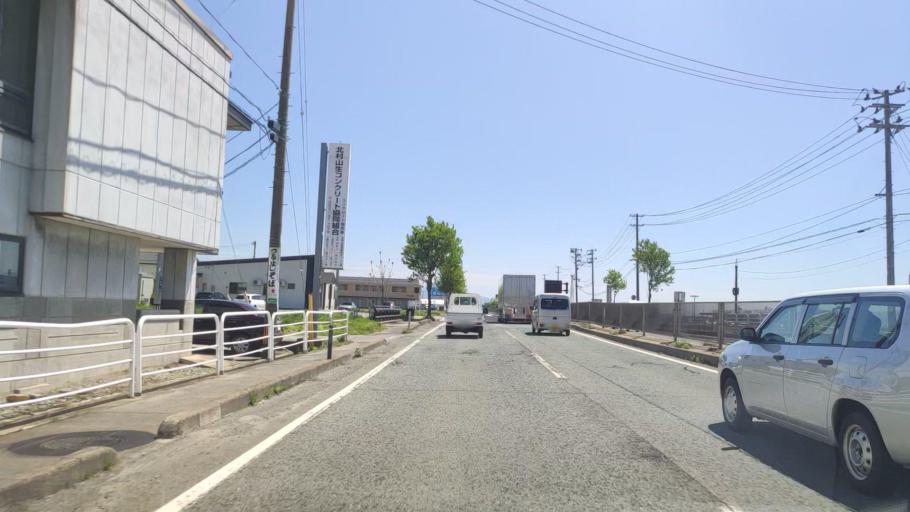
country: JP
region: Yamagata
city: Higashine
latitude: 38.4809
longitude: 140.3830
